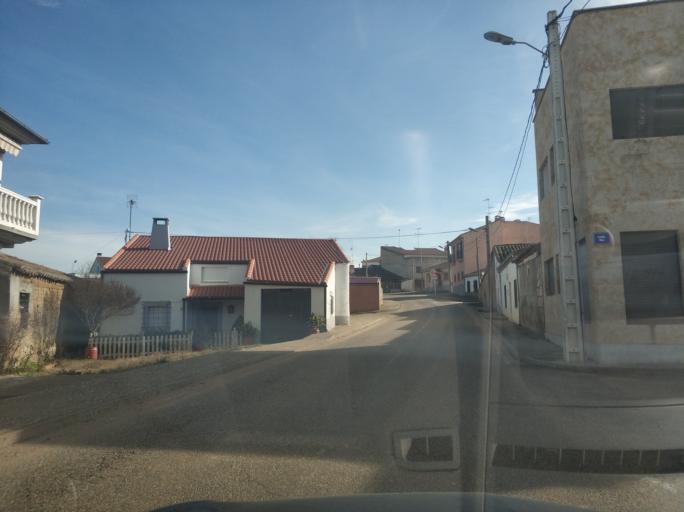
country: ES
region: Castille and Leon
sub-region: Provincia de Salamanca
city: Florida de Liebana
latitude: 41.0267
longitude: -5.7606
